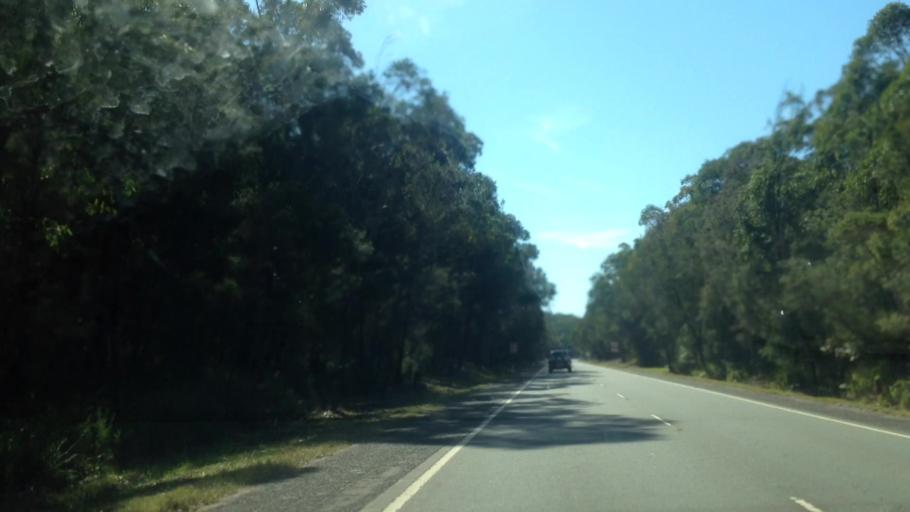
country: AU
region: New South Wales
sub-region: Lake Macquarie Shire
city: Toronto
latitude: -32.9869
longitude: 151.5107
